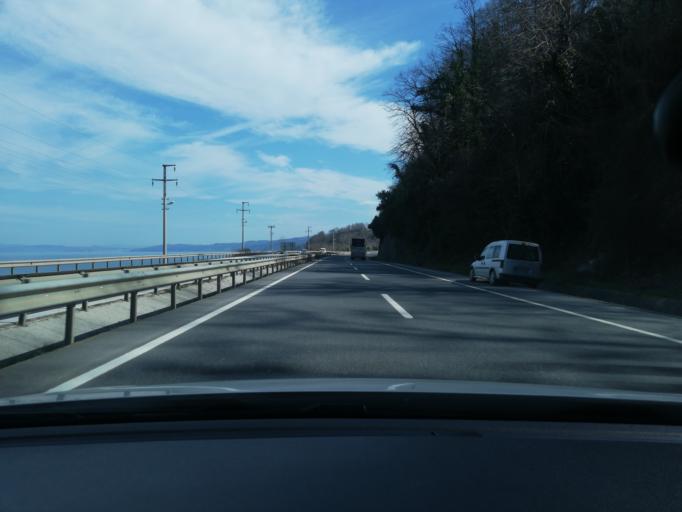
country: TR
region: Duzce
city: Akcakoca
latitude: 41.0966
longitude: 31.2079
